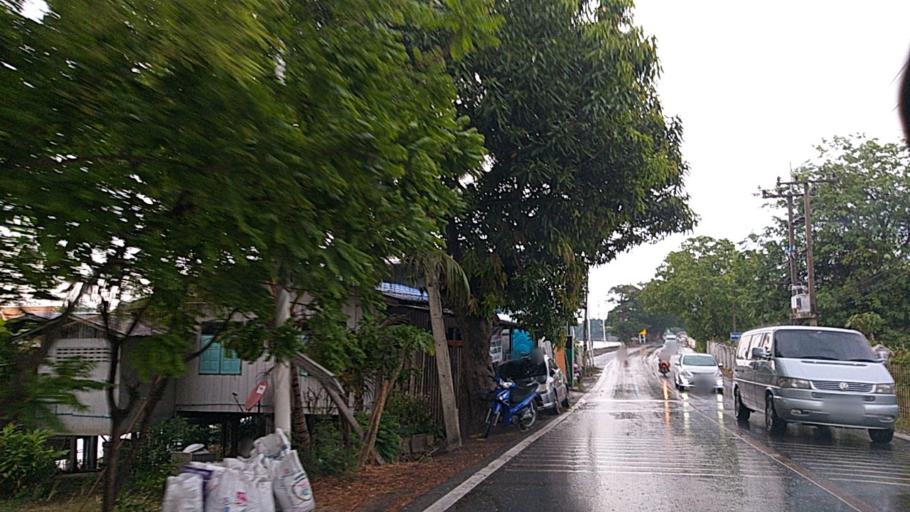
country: TH
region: Phra Nakhon Si Ayutthaya
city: Phra Nakhon Si Ayutthaya
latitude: 14.3501
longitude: 100.5460
